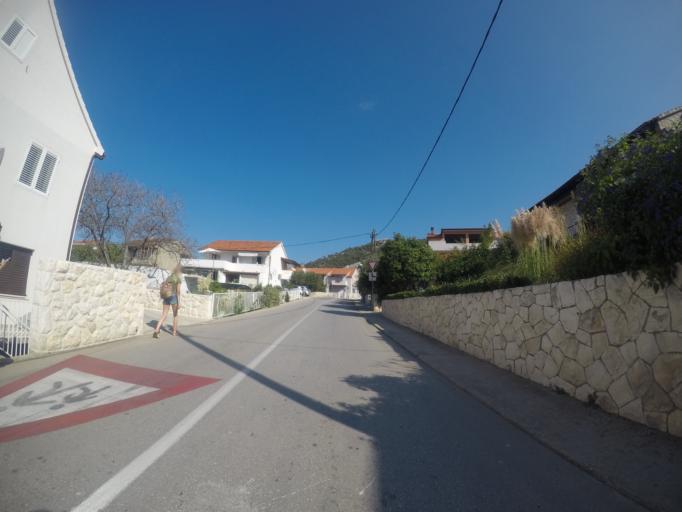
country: HR
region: Splitsko-Dalmatinska
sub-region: Grad Hvar
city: Hvar
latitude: 43.1700
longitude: 16.4463
